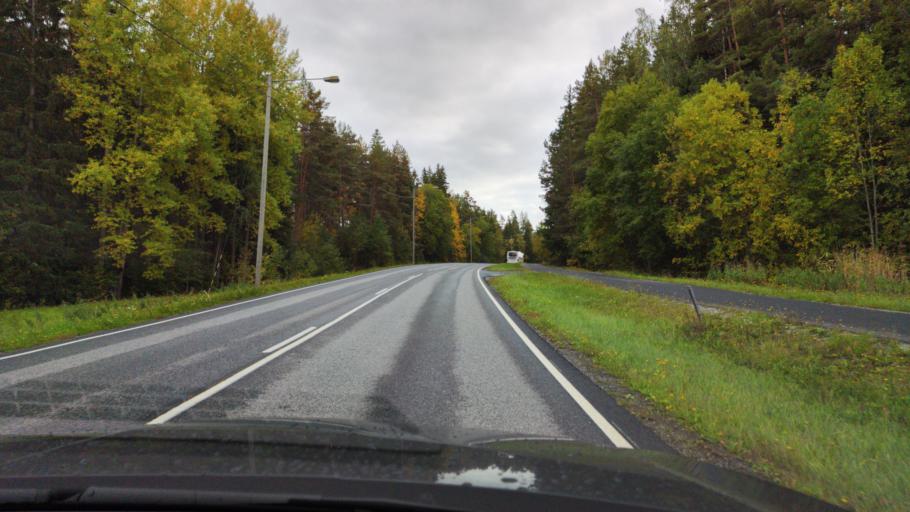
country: FI
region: Varsinais-Suomi
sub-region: Turku
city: Raisio
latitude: 60.3637
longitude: 22.1785
